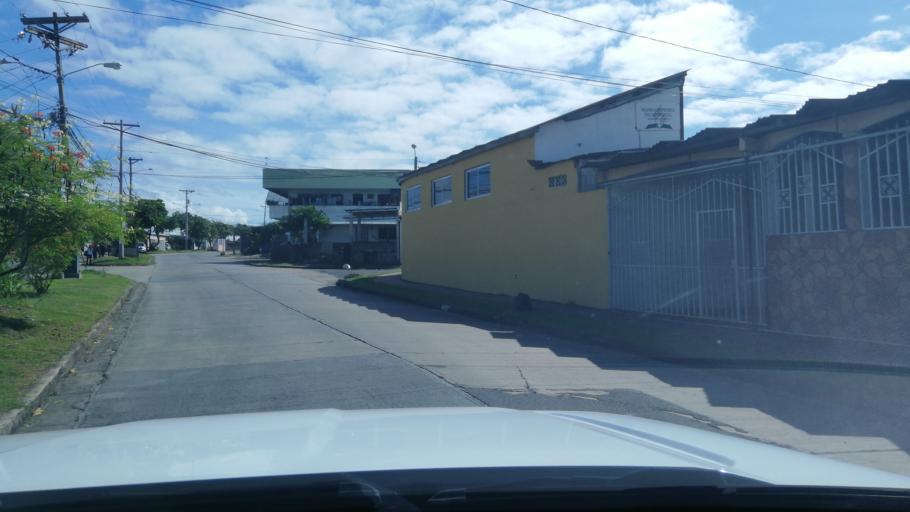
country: PA
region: Panama
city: Tocumen
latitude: 9.0783
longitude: -79.3604
